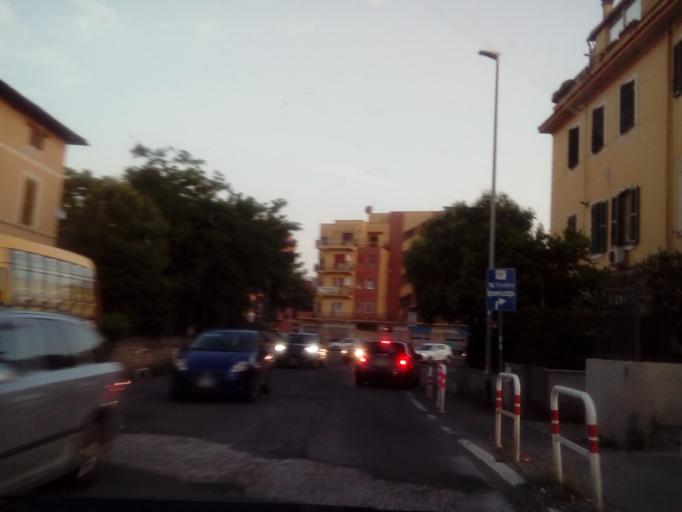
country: IT
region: Latium
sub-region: Citta metropolitana di Roma Capitale
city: Ciampino
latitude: 41.8689
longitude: 12.5877
